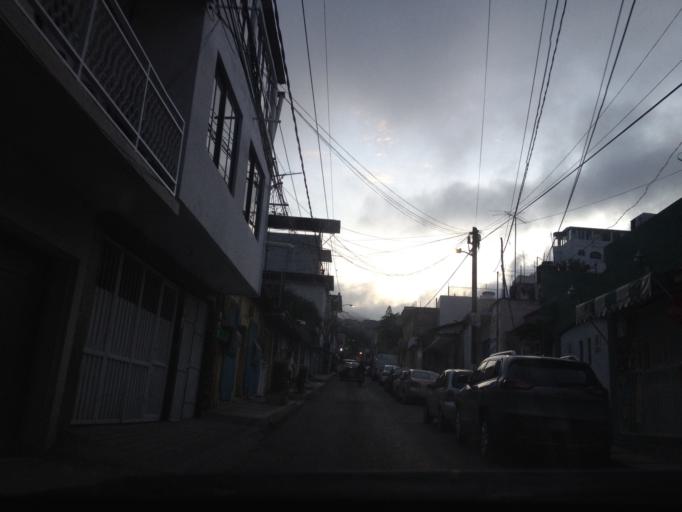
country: MX
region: Guerrero
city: Chilpancingo de los Bravos
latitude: 17.5578
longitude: -99.5029
